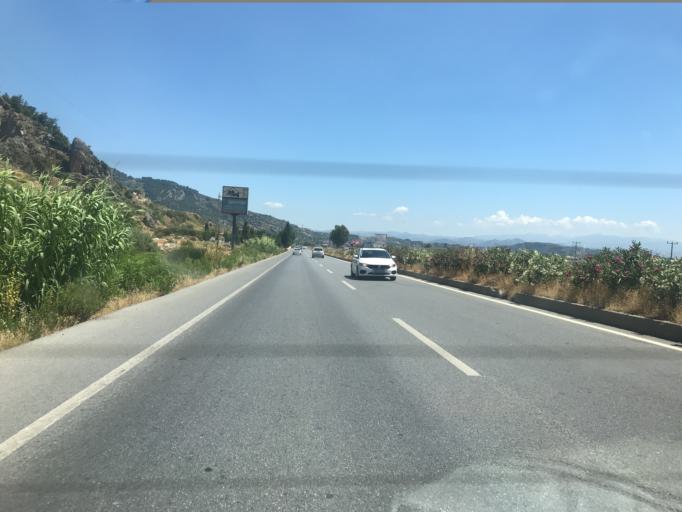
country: TR
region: Aydin
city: Ortaklar
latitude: 37.8098
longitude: 27.4812
